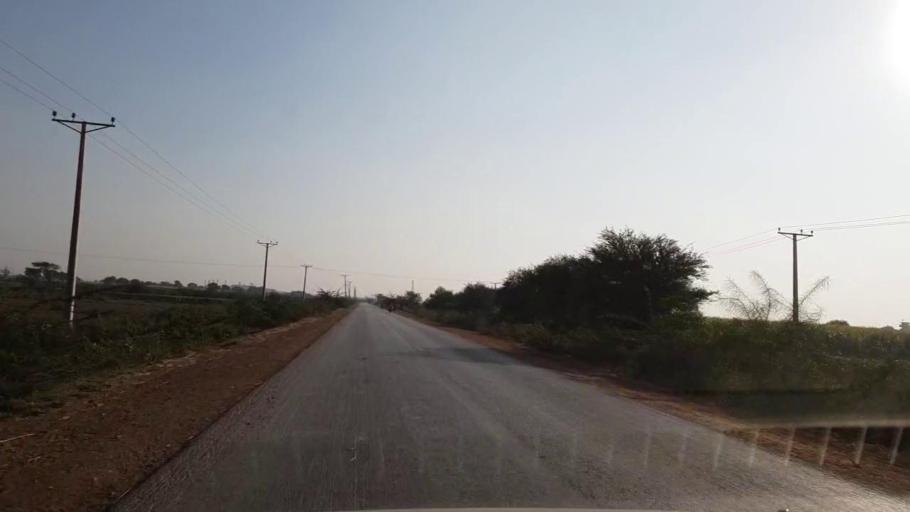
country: PK
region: Sindh
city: Bulri
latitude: 24.8249
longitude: 68.3225
